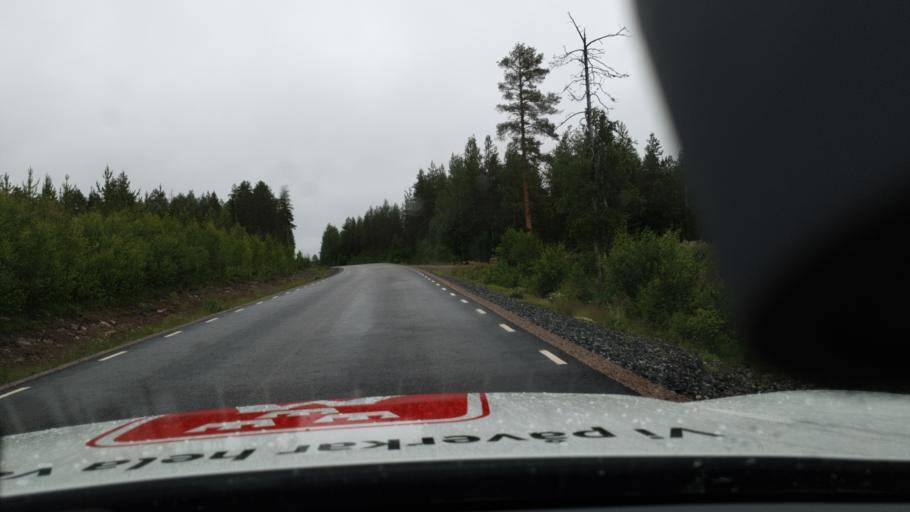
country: SE
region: Norrbotten
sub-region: Overtornea Kommun
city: OEvertornea
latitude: 66.5683
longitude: 23.3325
